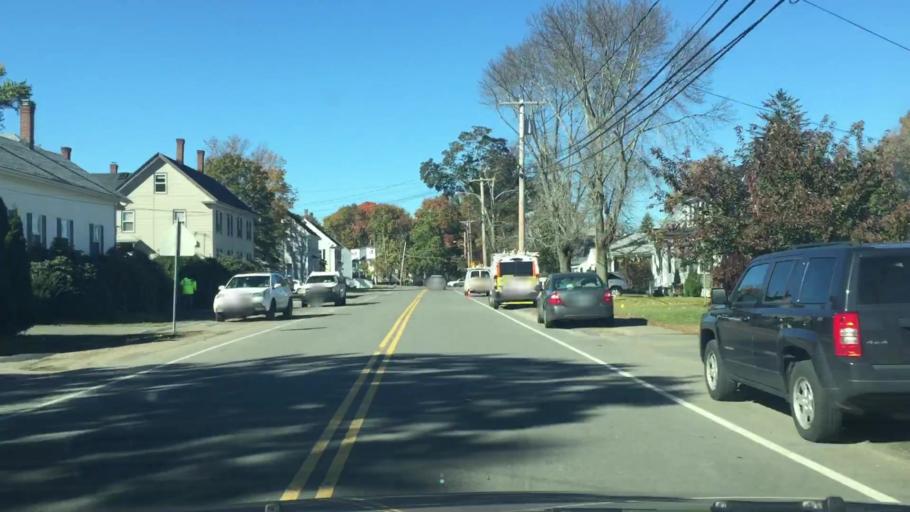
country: US
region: Massachusetts
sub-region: Essex County
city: North Andover
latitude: 42.6971
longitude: -71.1213
